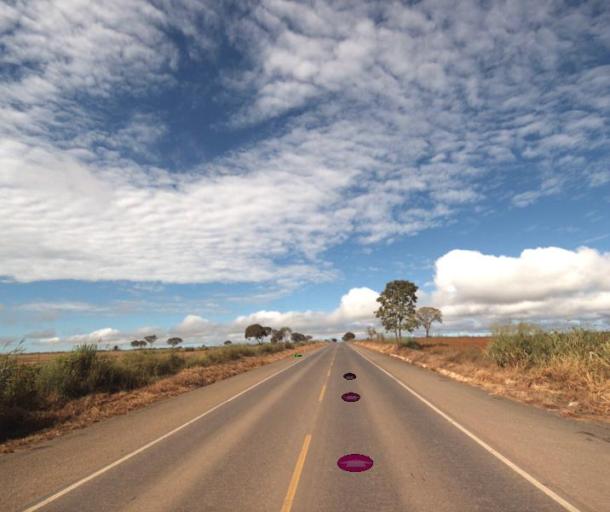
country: BR
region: Goias
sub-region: Uruacu
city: Uruacu
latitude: -14.7028
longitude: -49.2202
